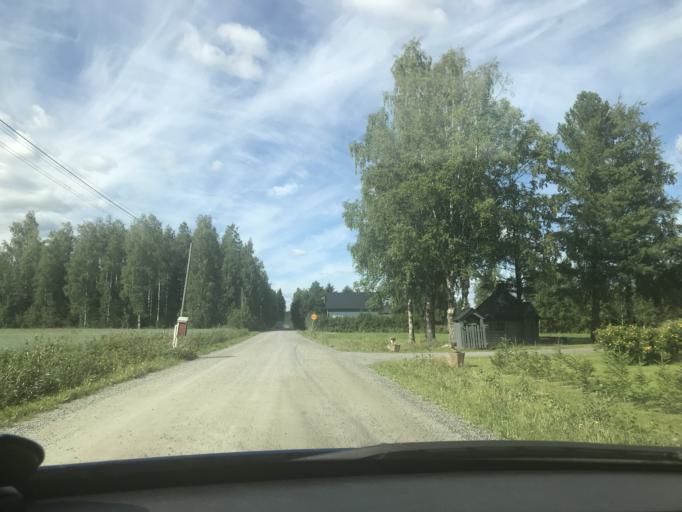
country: FI
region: Southern Ostrobothnia
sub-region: Kuusiokunnat
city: Alavus
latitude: 62.5892
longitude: 23.5826
